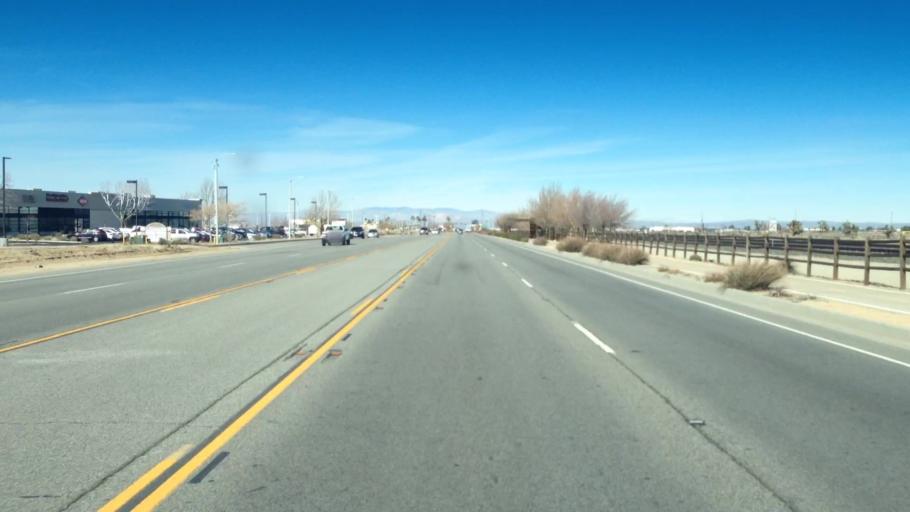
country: US
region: California
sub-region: Los Angeles County
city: Desert View Highlands
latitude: 34.6384
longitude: -118.1271
